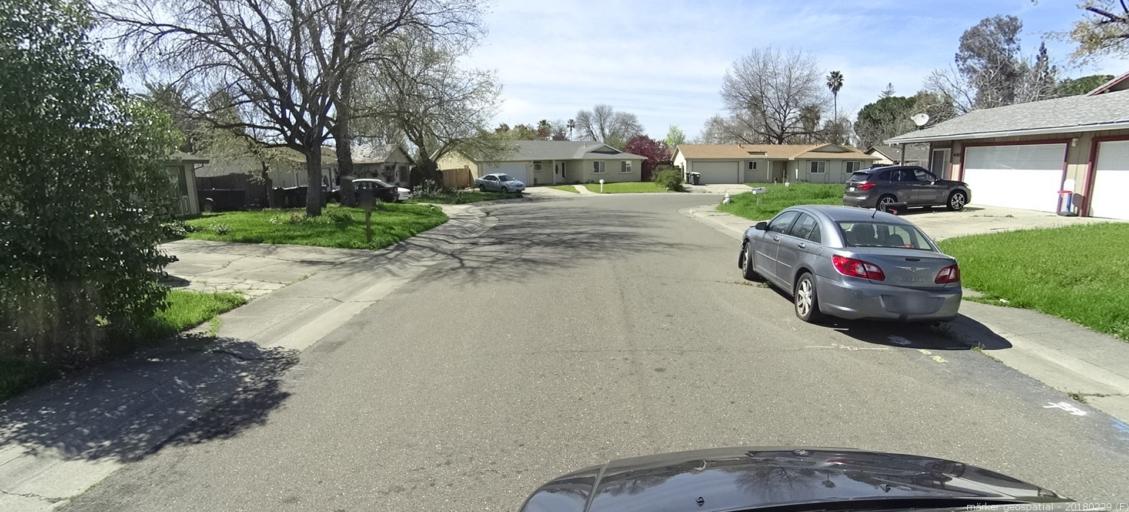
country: US
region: California
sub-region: Sacramento County
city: Rosemont
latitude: 38.5404
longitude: -121.3543
